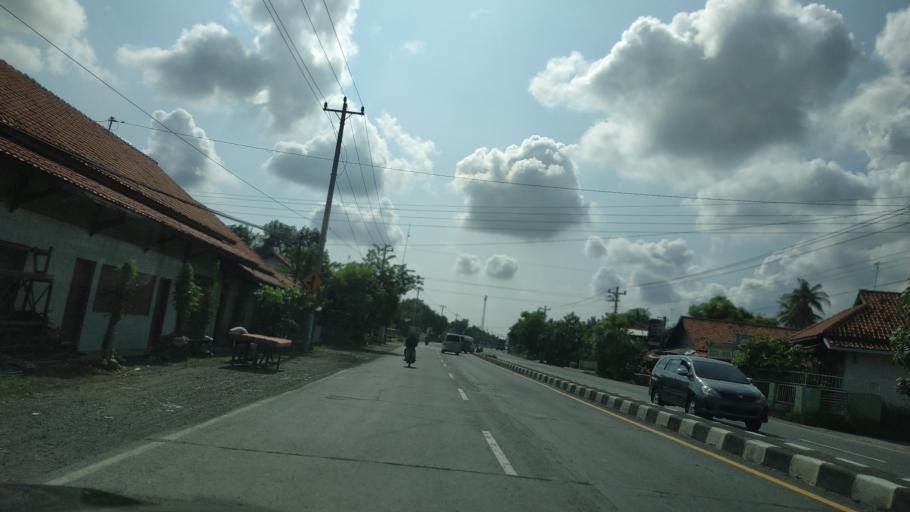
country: ID
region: Central Java
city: Comal
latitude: -6.8875
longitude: 109.5486
